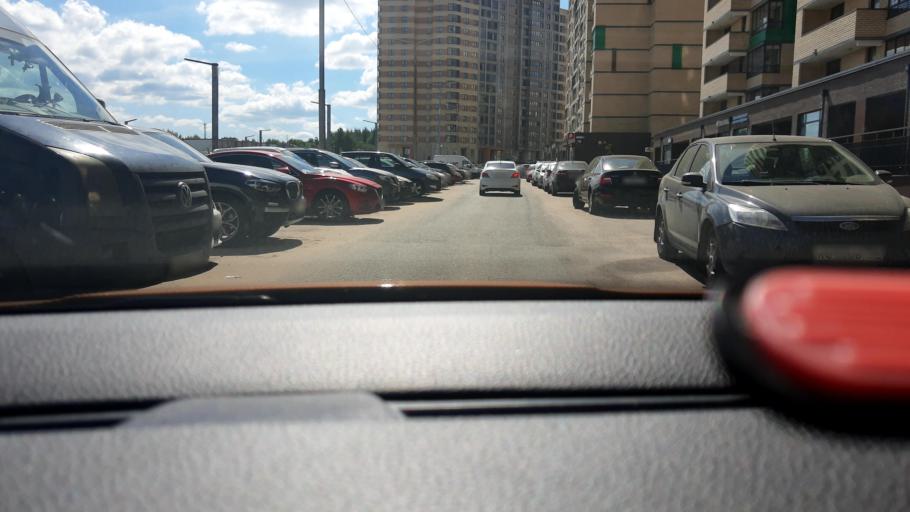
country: RU
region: Moskovskaya
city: Mytishchi
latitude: 55.9268
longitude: 37.7299
